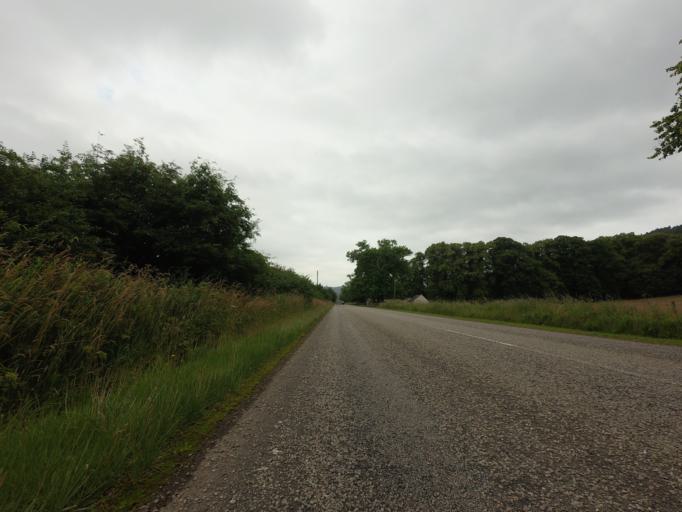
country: GB
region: Scotland
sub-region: Highland
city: Alness
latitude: 57.9131
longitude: -4.3797
